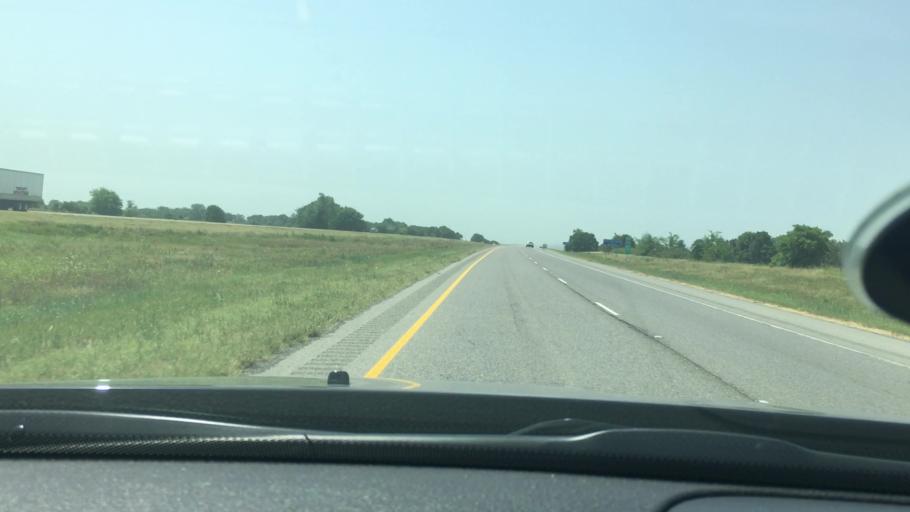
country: US
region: Oklahoma
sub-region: Garvin County
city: Wynnewood
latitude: 34.5605
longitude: -97.1940
